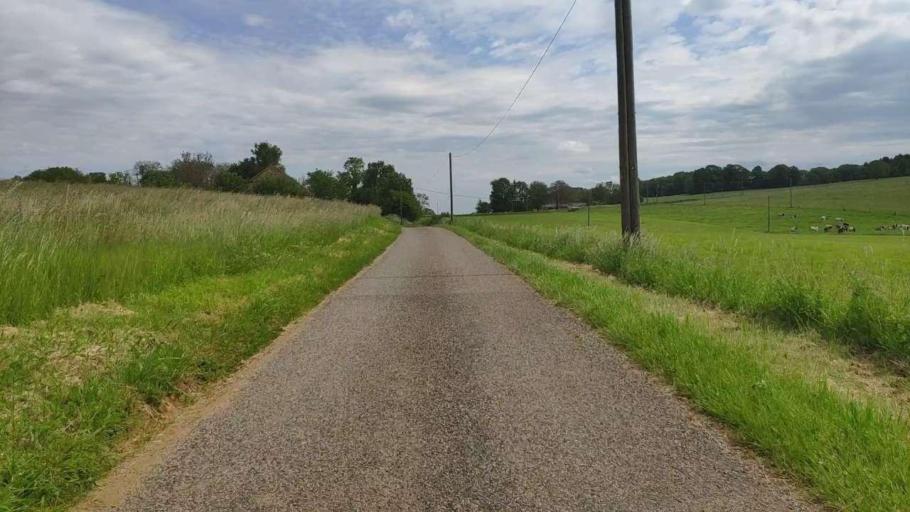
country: FR
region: Franche-Comte
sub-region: Departement du Jura
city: Poligny
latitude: 46.7907
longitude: 5.6424
